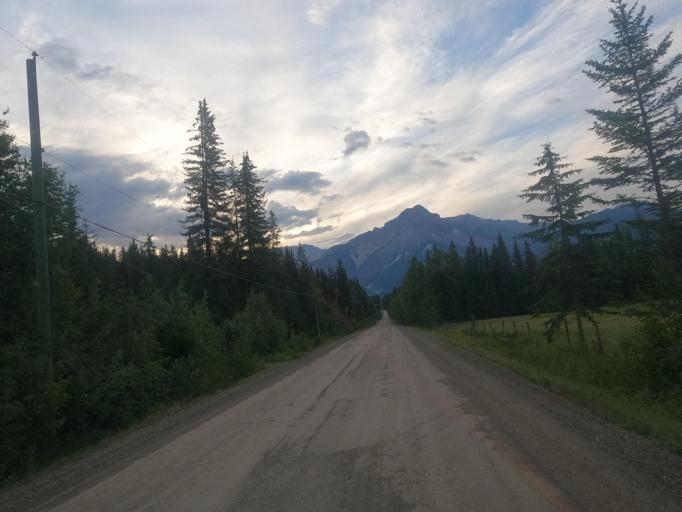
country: CA
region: British Columbia
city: Golden
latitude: 51.4384
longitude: -117.0527
